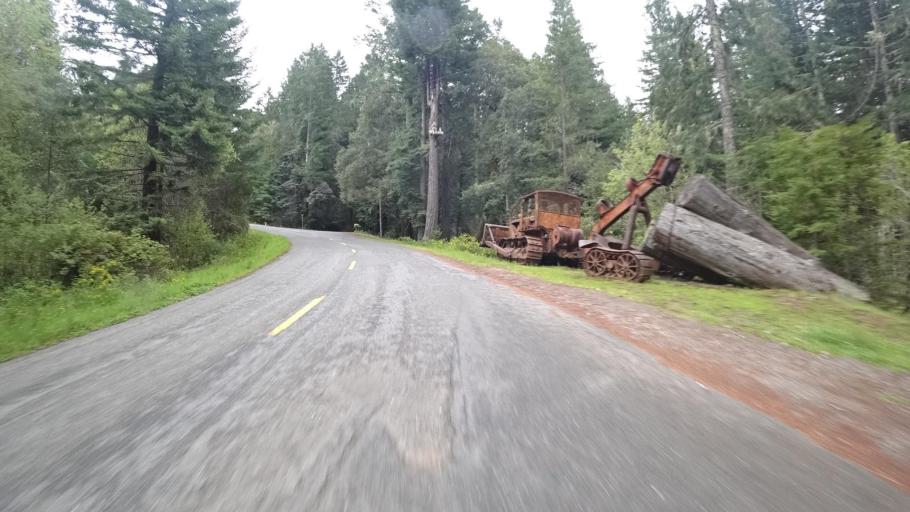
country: US
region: California
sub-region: Humboldt County
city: Redway
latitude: 40.2786
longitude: -123.7957
